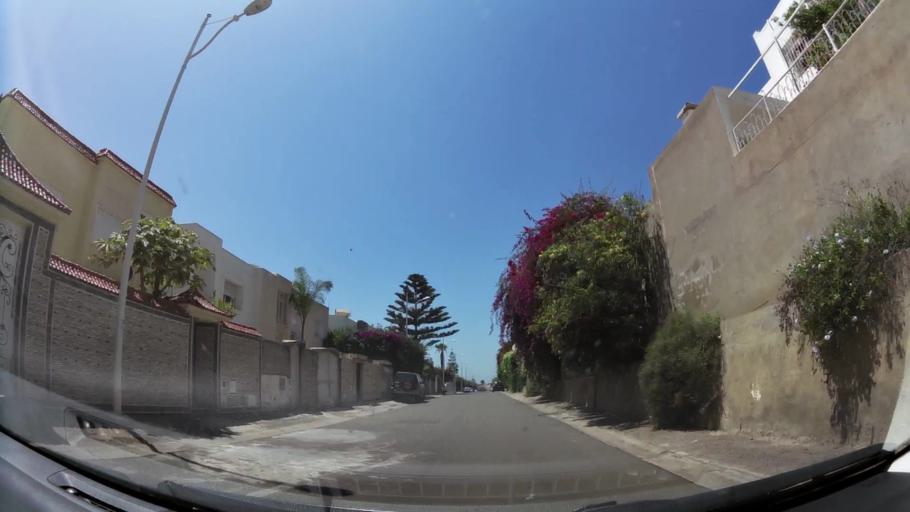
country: MA
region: Souss-Massa-Draa
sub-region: Agadir-Ida-ou-Tnan
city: Agadir
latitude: 30.4343
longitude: -9.5836
